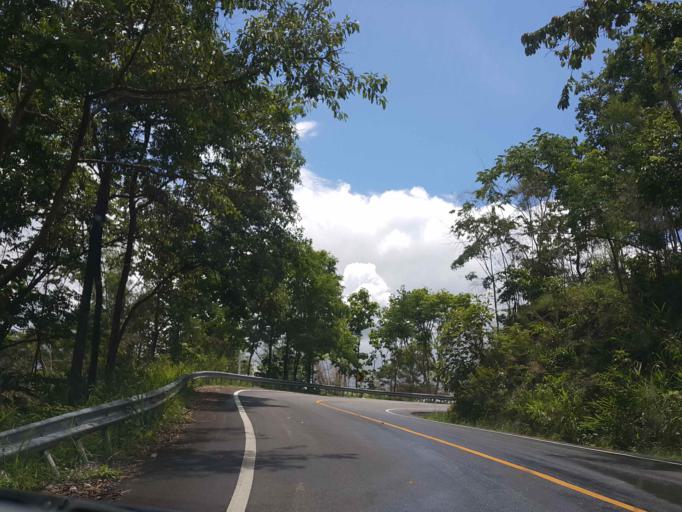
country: TH
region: Chiang Mai
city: Samoeng
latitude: 18.8496
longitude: 98.7718
